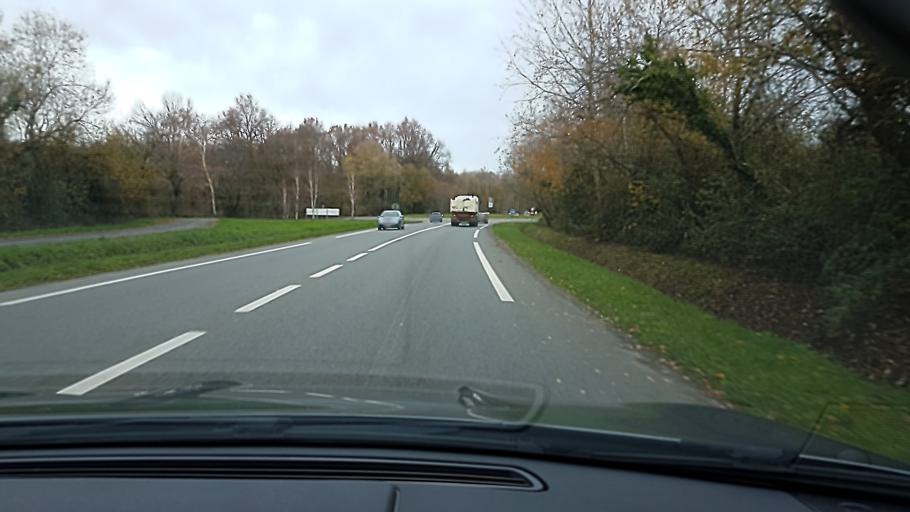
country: FR
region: Aquitaine
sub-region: Departement des Pyrenees-Atlantiques
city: Idron
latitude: 43.3060
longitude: -0.3080
